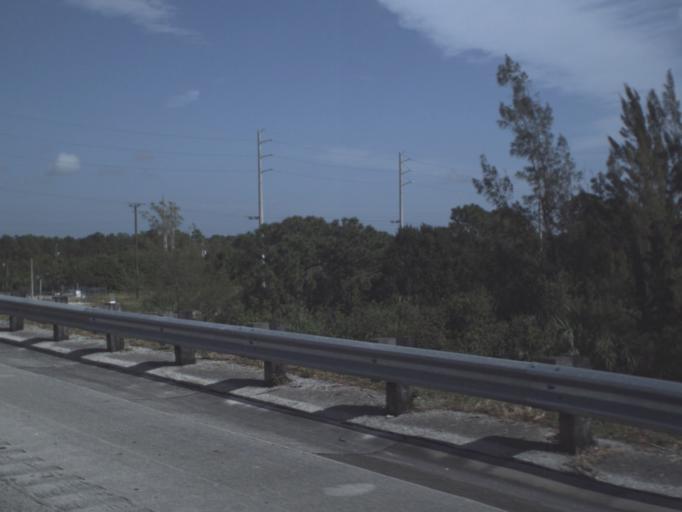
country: US
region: Florida
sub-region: Saint Lucie County
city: Fort Pierce South
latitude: 27.3789
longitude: -80.3860
